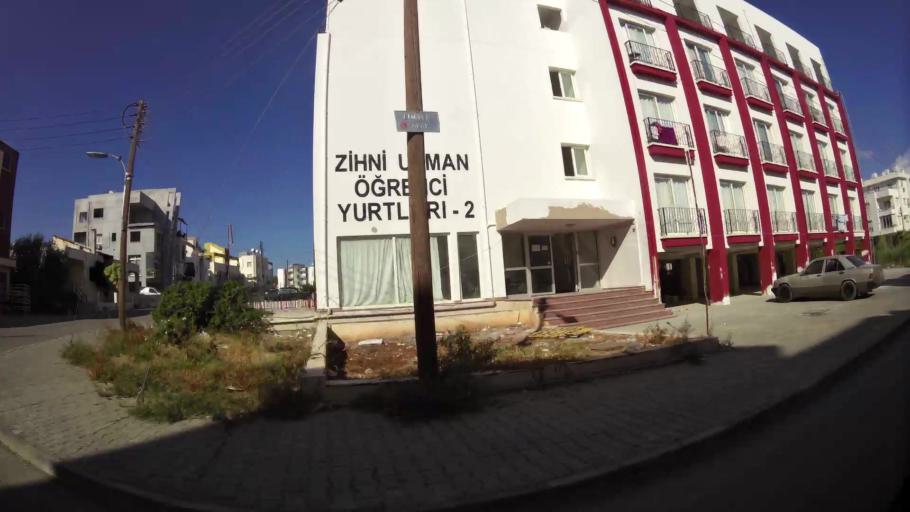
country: CY
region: Lefkosia
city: Nicosia
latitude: 35.2116
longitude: 33.3154
